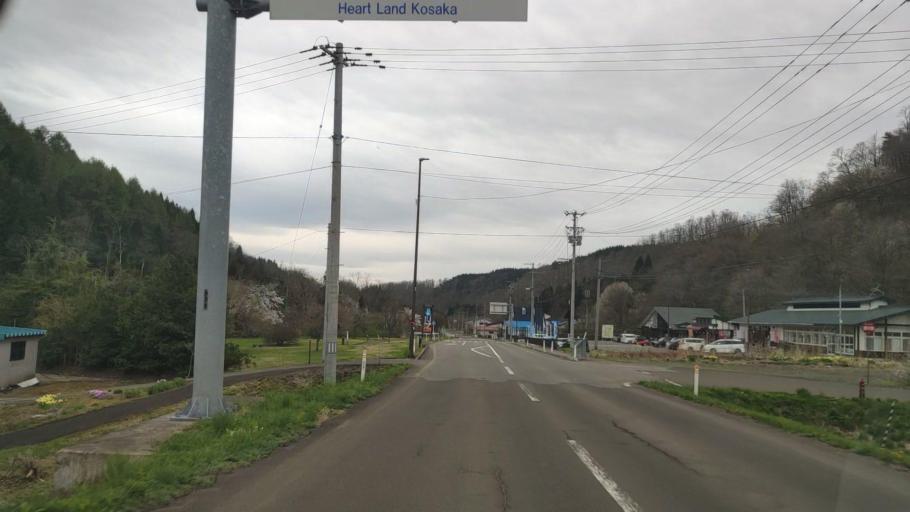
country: JP
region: Akita
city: Hanawa
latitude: 40.3574
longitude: 140.7836
